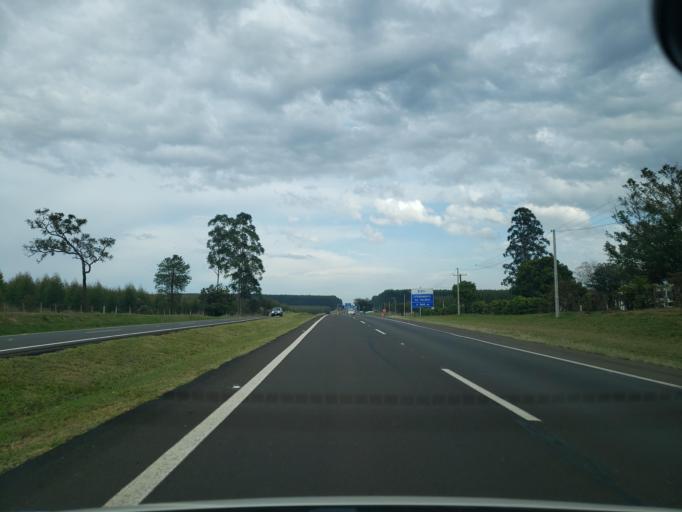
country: BR
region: Sao Paulo
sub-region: Itirapina
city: Itirapina
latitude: -22.2602
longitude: -47.8792
